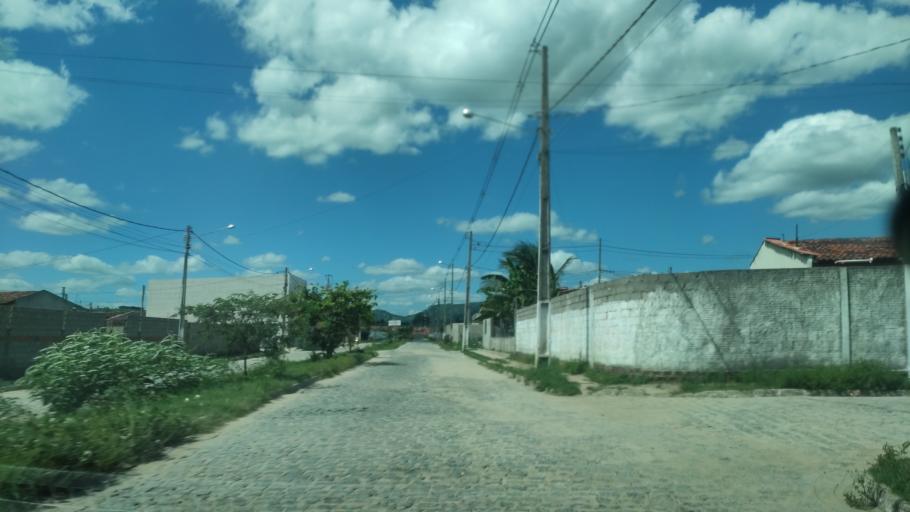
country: BR
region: Alagoas
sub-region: Uniao Dos Palmares
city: Uniao dos Palmares
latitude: -9.1476
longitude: -36.0039
